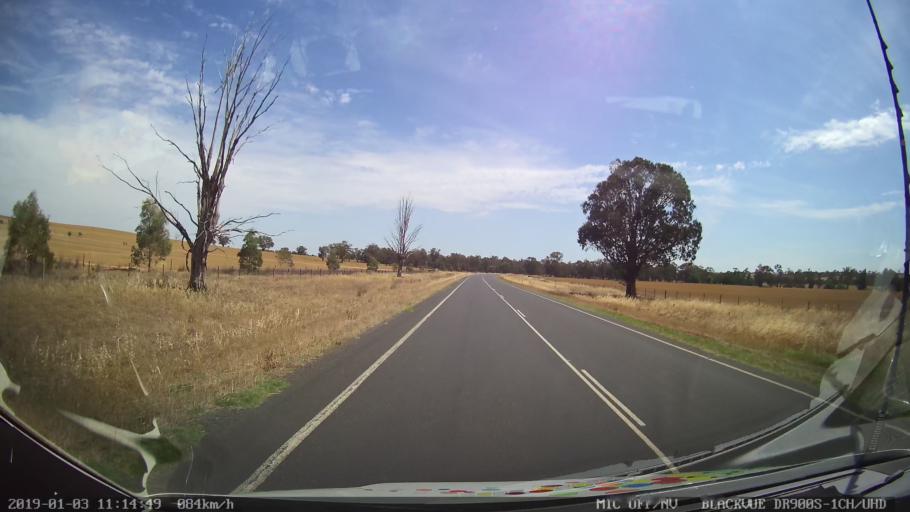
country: AU
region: New South Wales
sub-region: Young
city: Young
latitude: -34.1713
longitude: 148.2614
